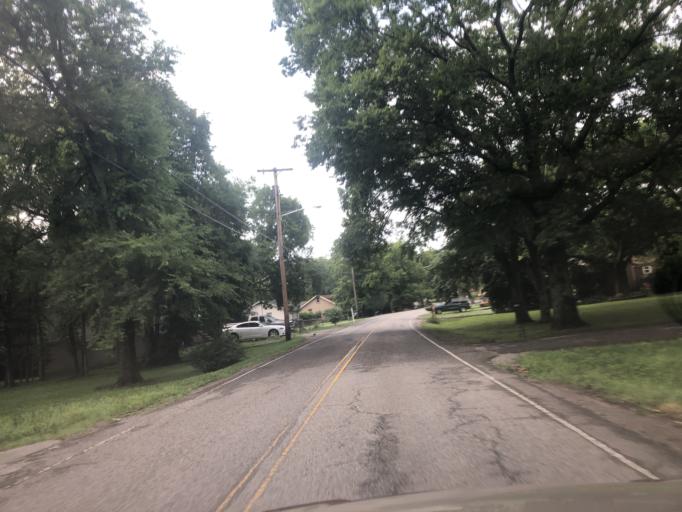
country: US
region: Tennessee
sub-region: Davidson County
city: Goodlettsville
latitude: 36.2539
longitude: -86.7075
